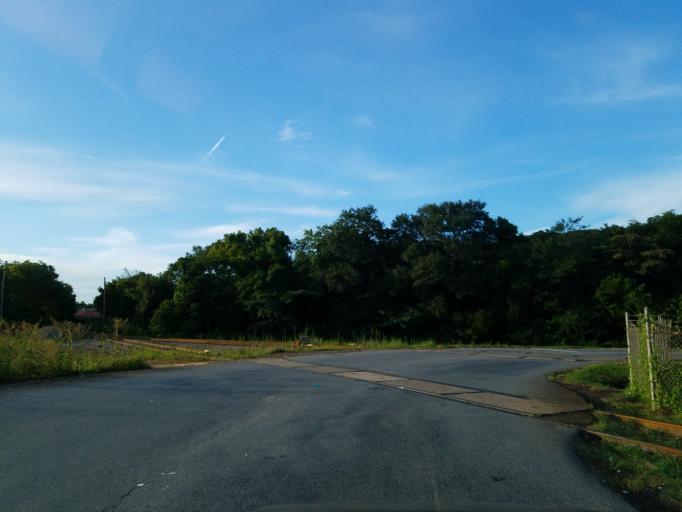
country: US
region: Georgia
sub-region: Bartow County
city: Cartersville
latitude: 34.1522
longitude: -84.7876
